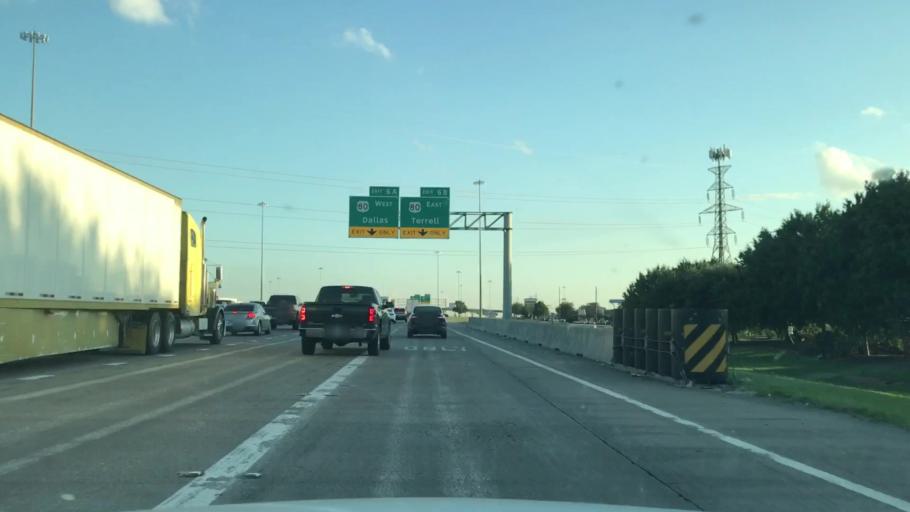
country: US
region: Texas
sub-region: Dallas County
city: Mesquite
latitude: 32.8012
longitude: -96.6266
